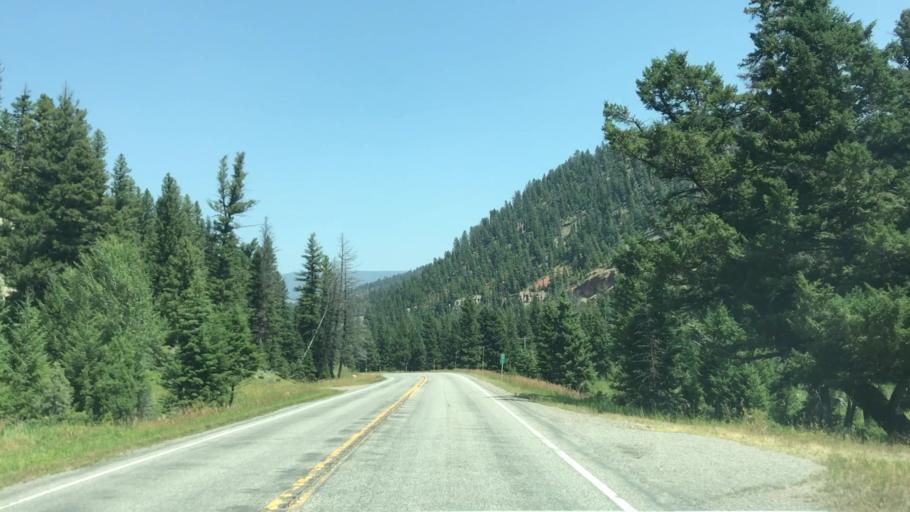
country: US
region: Montana
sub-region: Gallatin County
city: Big Sky
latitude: 45.1670
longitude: -111.2457
